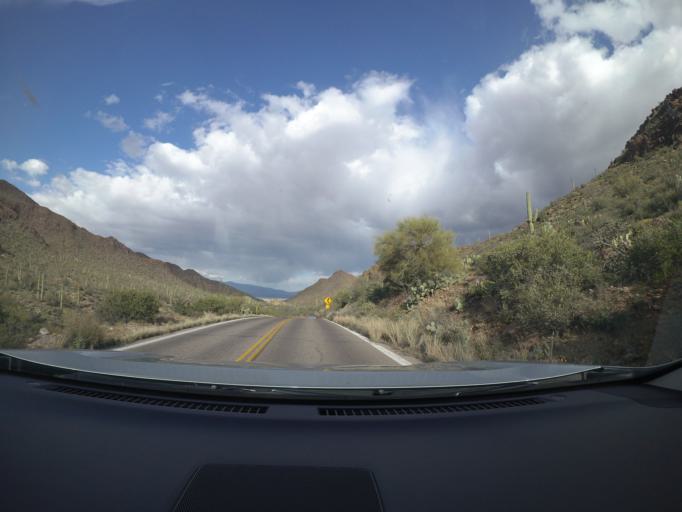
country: US
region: Arizona
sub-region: Pima County
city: Tucson Estates
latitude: 32.2236
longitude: -111.0966
